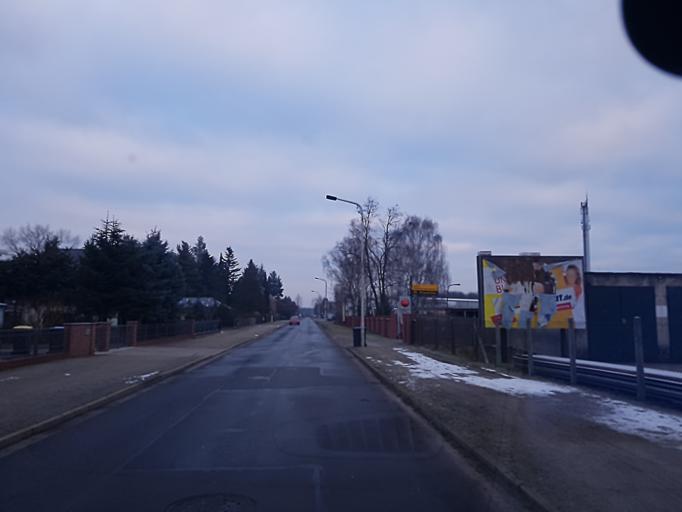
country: DE
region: Brandenburg
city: Finsterwalde
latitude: 51.6408
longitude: 13.7085
